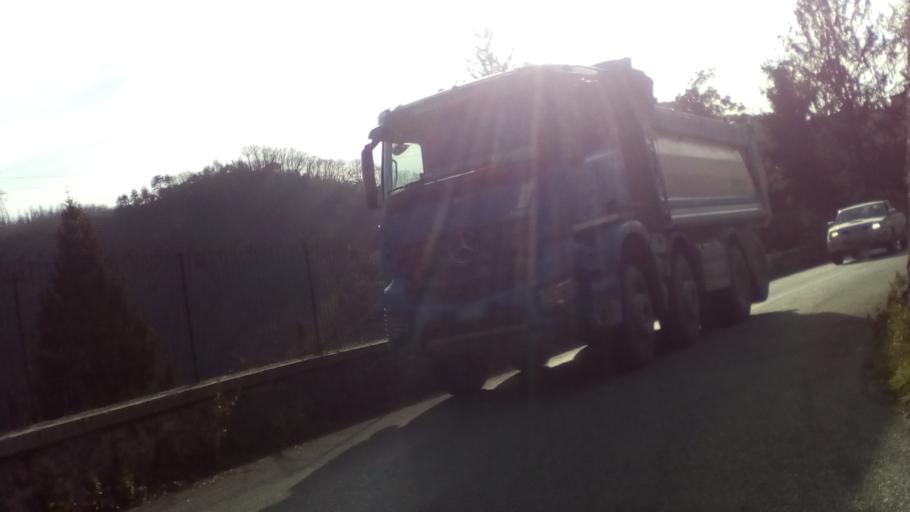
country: IT
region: Tuscany
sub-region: Provincia di Massa-Carrara
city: Massa
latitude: 44.0840
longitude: 10.1171
